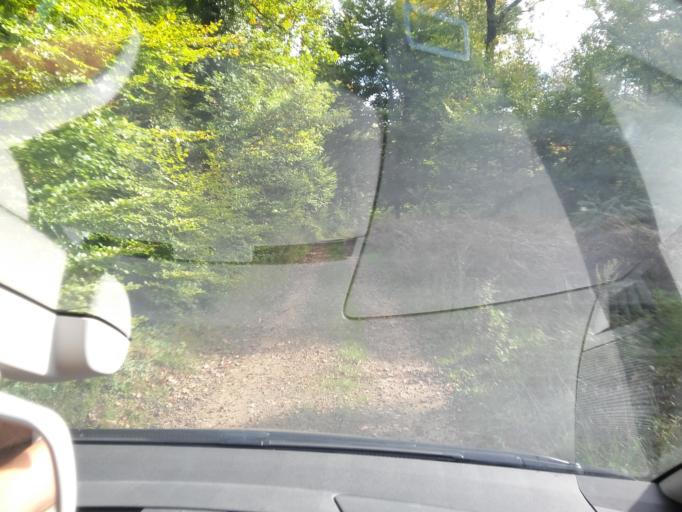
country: BE
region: Wallonia
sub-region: Province du Luxembourg
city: Attert
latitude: 49.7202
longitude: 5.7829
